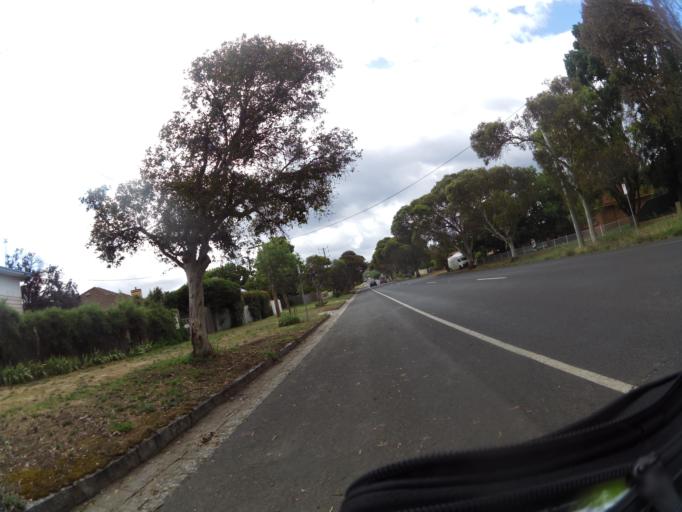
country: AU
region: Victoria
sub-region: Mount Alexander
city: Castlemaine
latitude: -37.0696
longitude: 144.1996
